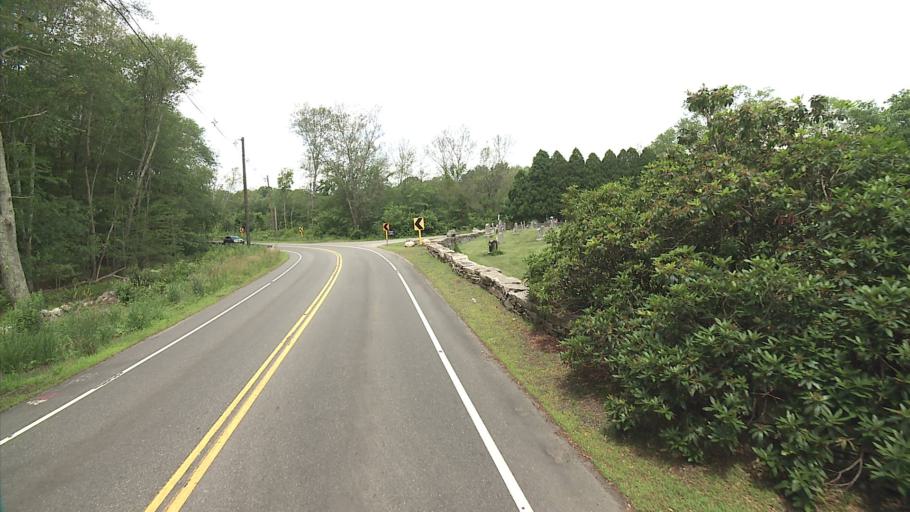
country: US
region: Connecticut
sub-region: New London County
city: Ledyard Center
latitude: 41.4510
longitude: -72.0501
